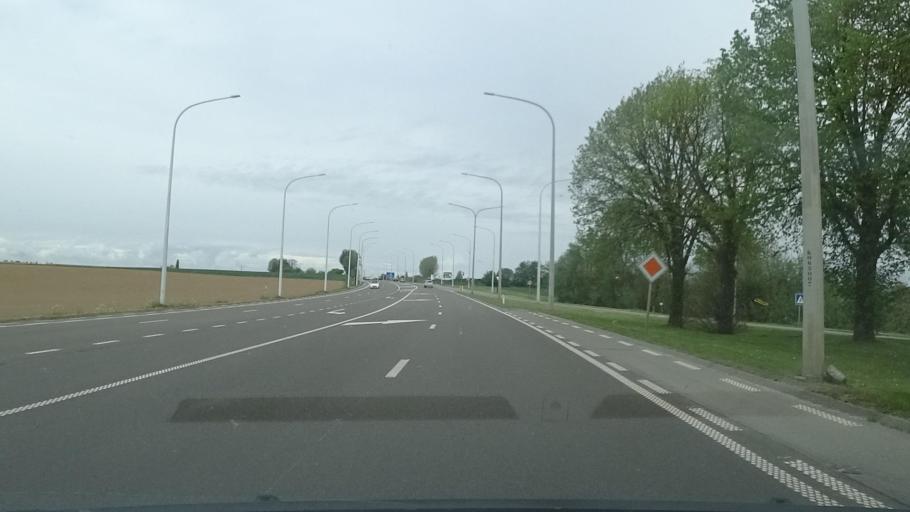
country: BE
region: Wallonia
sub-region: Province de Namur
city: Floreffe
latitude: 50.5136
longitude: 4.7729
